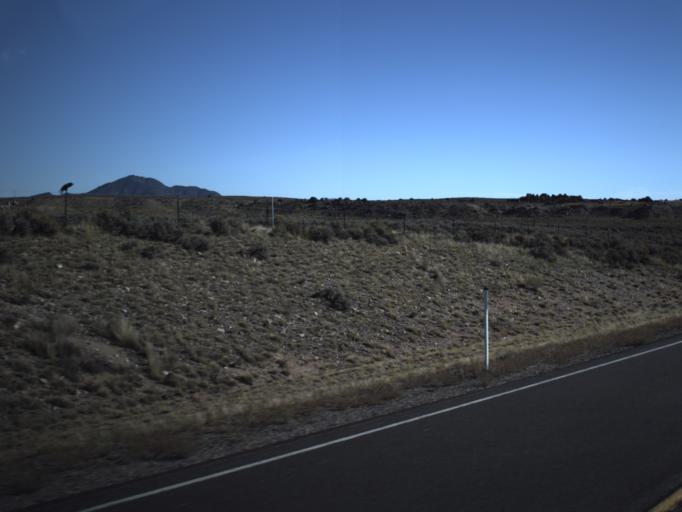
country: US
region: Utah
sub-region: Washington County
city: Enterprise
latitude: 37.7247
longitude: -114.0388
